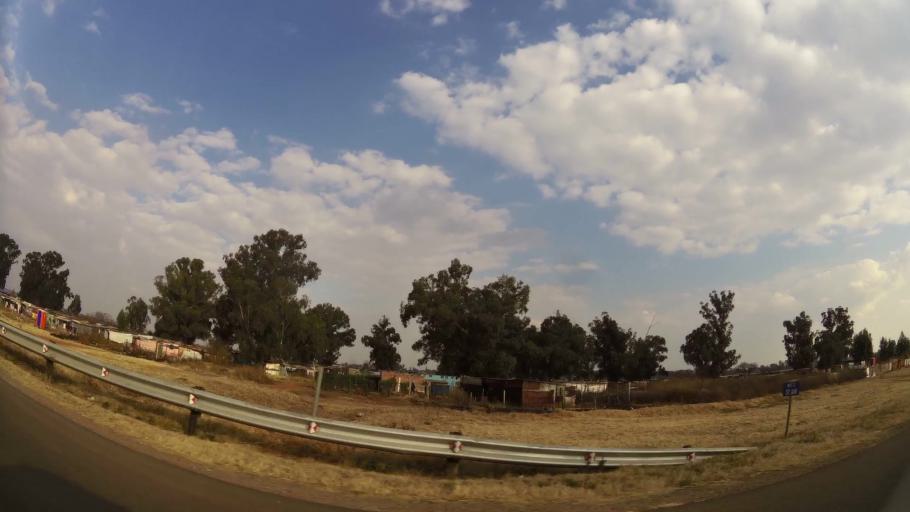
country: ZA
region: Gauteng
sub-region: Ekurhuleni Metropolitan Municipality
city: Springs
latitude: -26.2722
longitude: 28.4784
